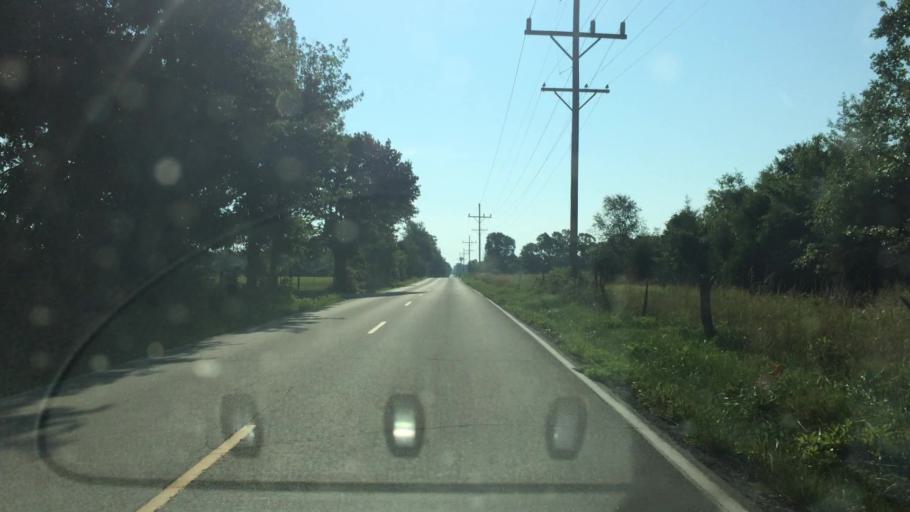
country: US
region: Missouri
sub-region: Greene County
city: Strafford
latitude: 37.2712
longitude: -93.1479
